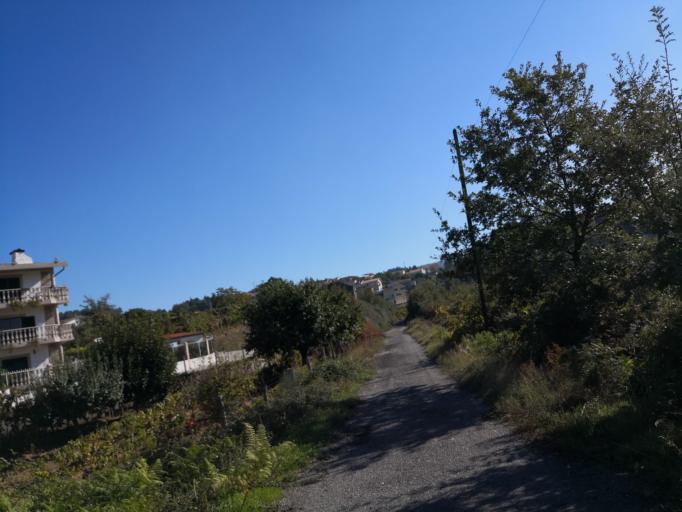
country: PT
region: Vila Real
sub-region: Vila Real
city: Vila Real
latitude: 41.3024
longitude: -7.7253
